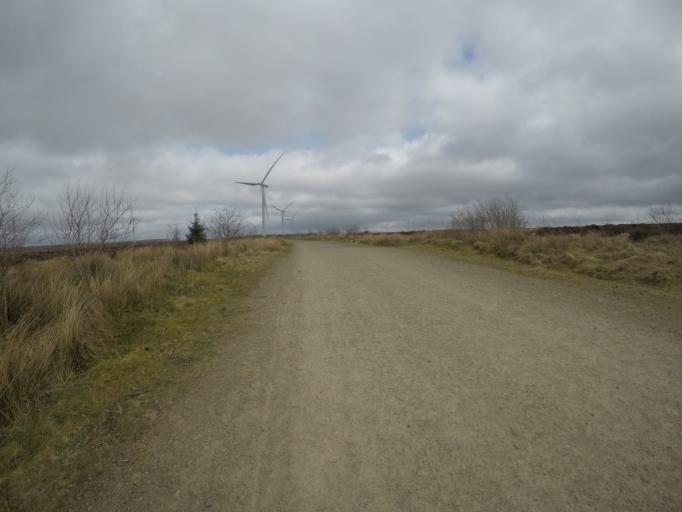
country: GB
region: Scotland
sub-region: East Renfrewshire
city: Newton Mearns
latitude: 55.6980
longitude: -4.3441
